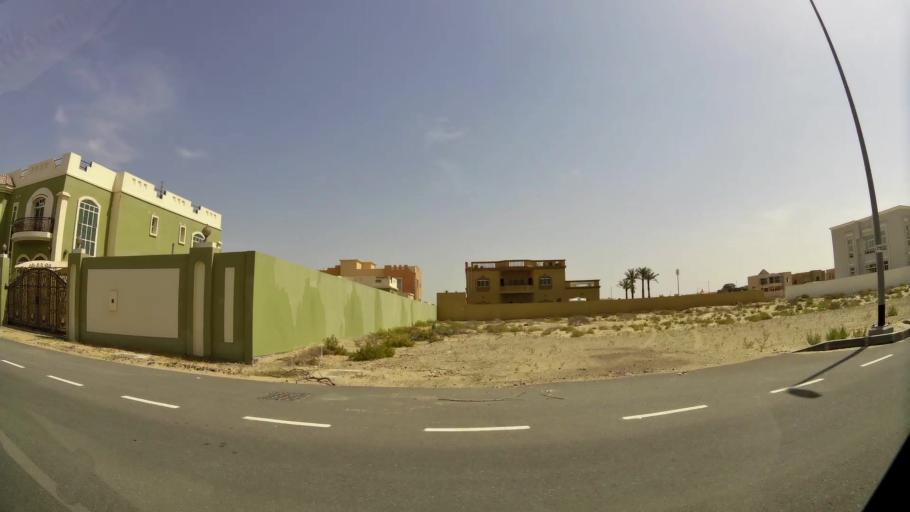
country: AE
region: Ash Shariqah
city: Sharjah
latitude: 25.1872
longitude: 55.4304
